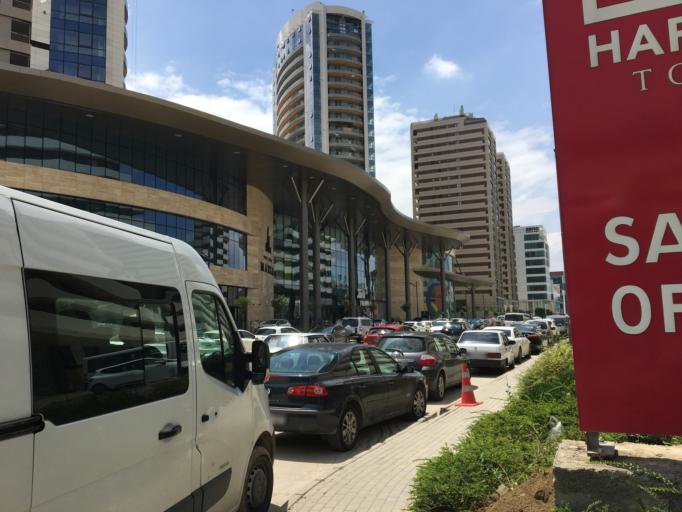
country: TR
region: Bursa
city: Yildirim
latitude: 40.2082
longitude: 28.9971
